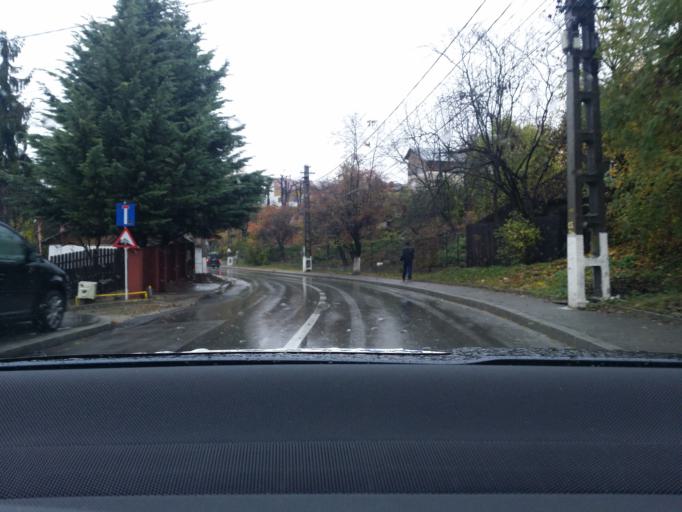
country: RO
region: Prahova
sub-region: Municipiul Campina
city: Campina
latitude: 45.1269
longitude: 25.7280
